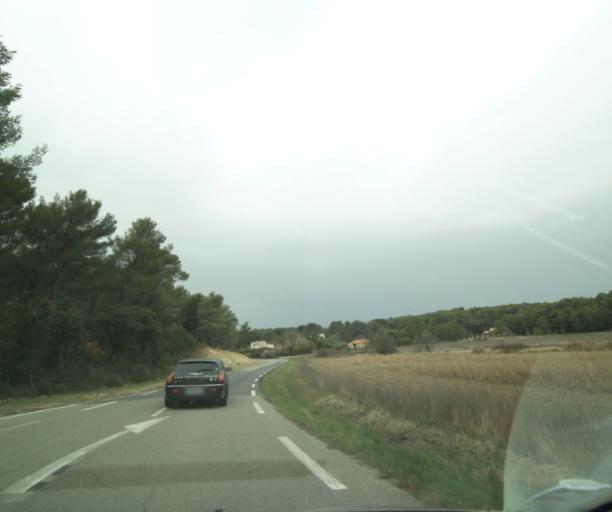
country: FR
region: Provence-Alpes-Cote d'Azur
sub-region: Departement des Bouches-du-Rhone
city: Saint-Marc-Jaumegarde
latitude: 43.5463
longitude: 5.5183
